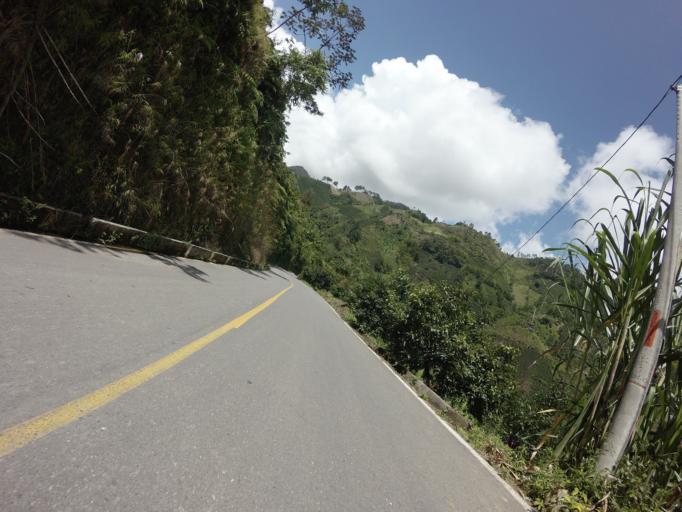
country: CO
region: Caldas
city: Marquetalia
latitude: 5.2901
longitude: -75.1046
